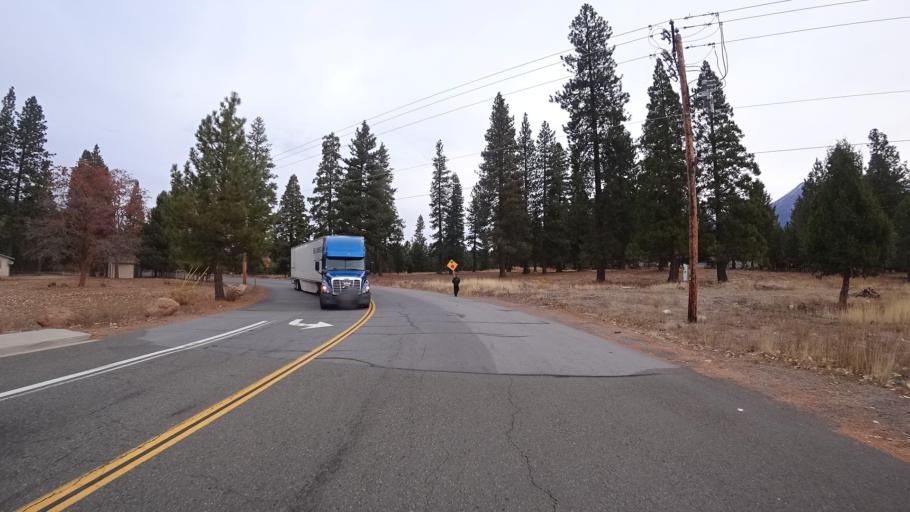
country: US
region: California
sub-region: Siskiyou County
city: Weed
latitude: 41.4000
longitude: -122.3796
